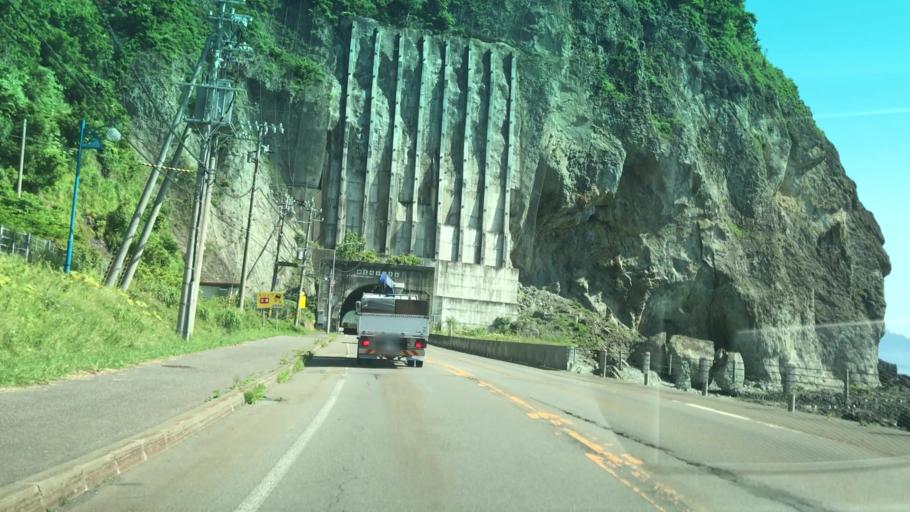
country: JP
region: Hokkaido
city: Iwanai
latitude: 43.1108
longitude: 140.4504
